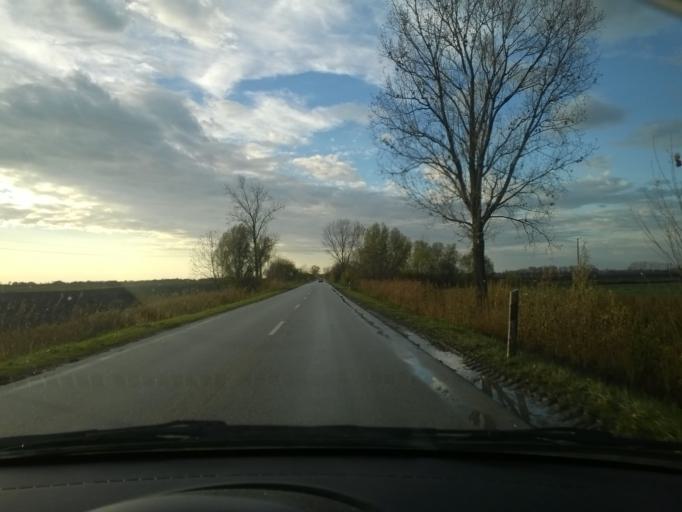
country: HU
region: Bacs-Kiskun
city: Kalocsa
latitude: 46.5087
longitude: 19.0284
